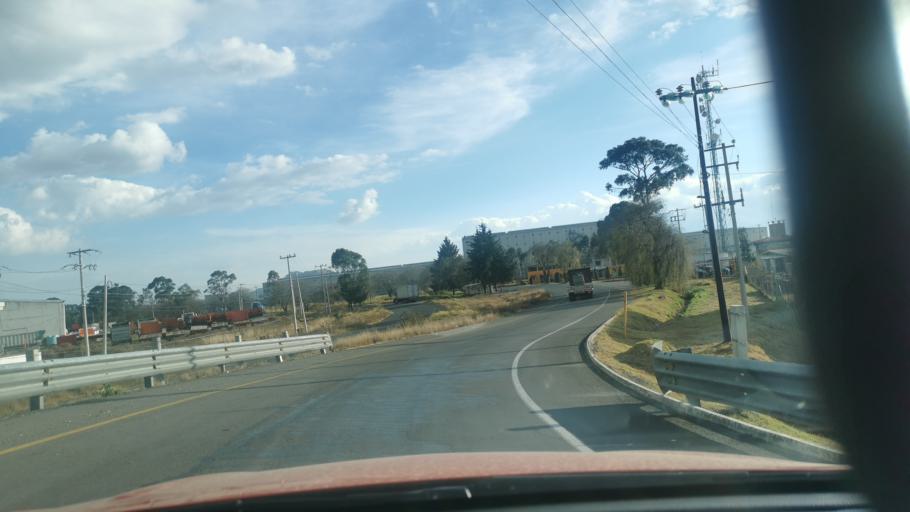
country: MX
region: Mexico
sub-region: Toluca
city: Colonia Aviacion Autopan
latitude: 19.3859
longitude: -99.7085
